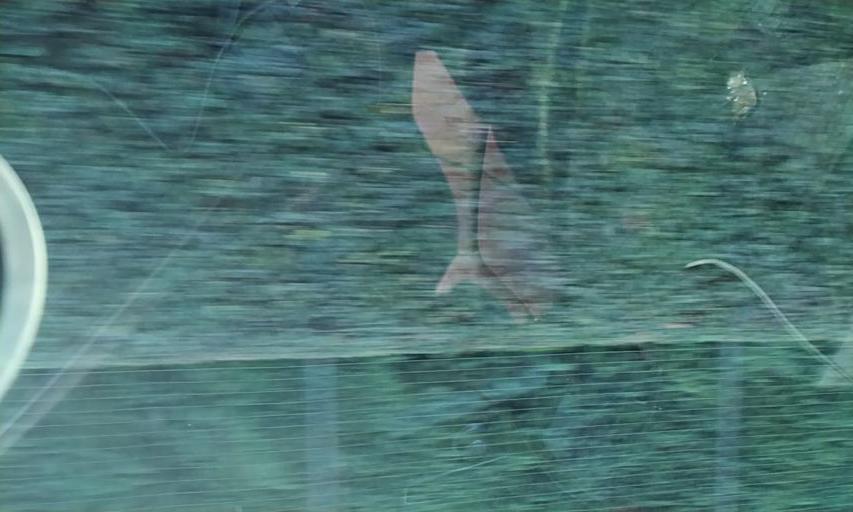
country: PT
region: Porto
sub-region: Trofa
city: Bougado
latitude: 41.3395
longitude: -8.5205
